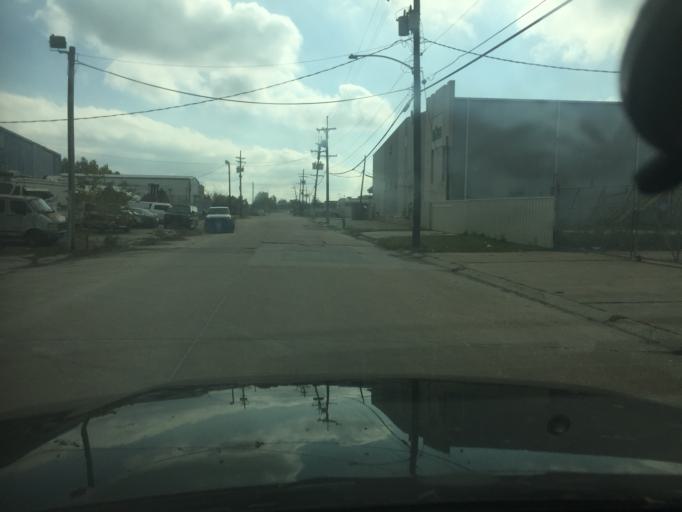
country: US
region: Louisiana
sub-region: Saint Bernard Parish
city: Arabi
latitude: 29.9979
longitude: -90.0326
